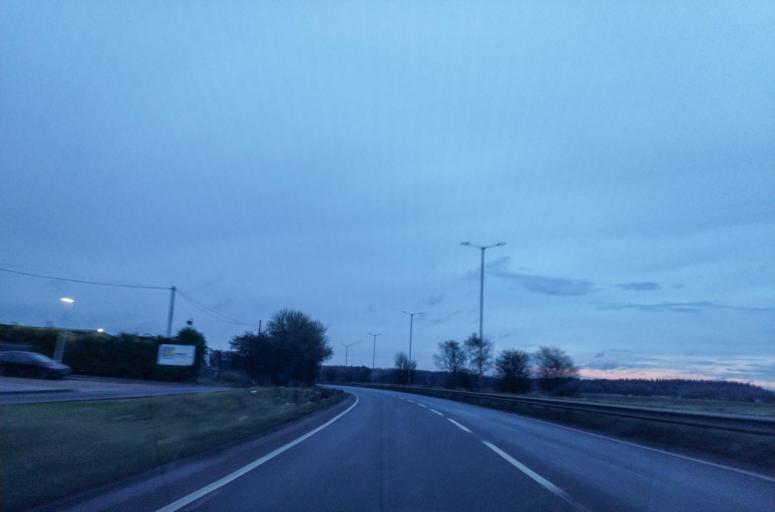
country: GB
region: England
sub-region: Kent
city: Boxley
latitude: 51.3009
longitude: 0.5983
